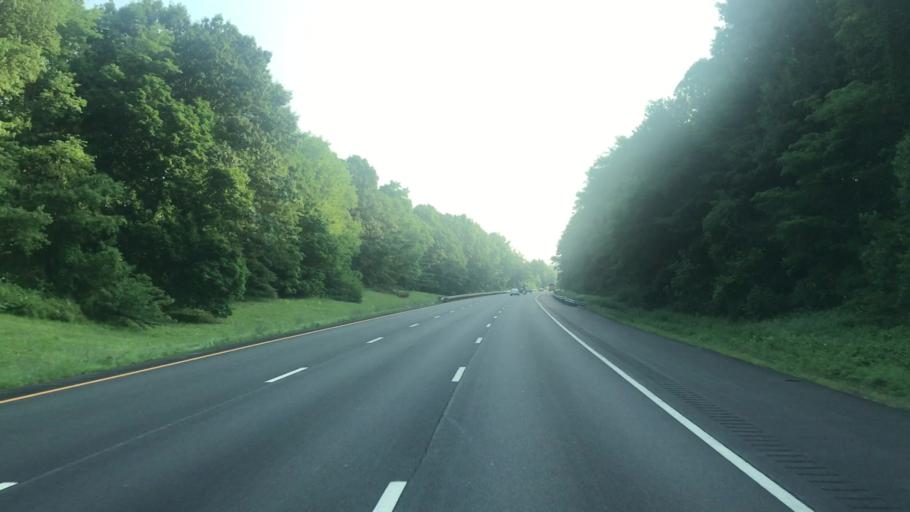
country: US
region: New York
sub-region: Westchester County
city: Bedford Hills
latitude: 41.2214
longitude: -73.6845
